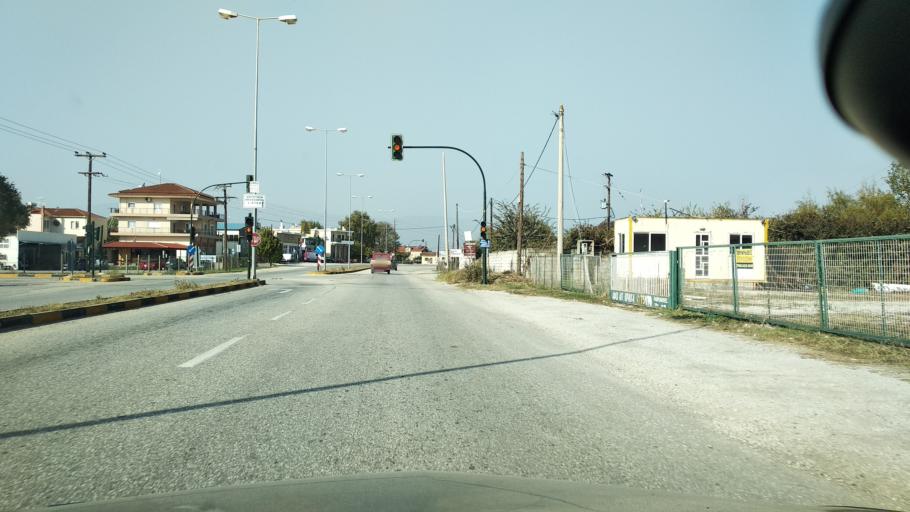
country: GR
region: Thessaly
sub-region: Trikala
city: Trikala
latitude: 39.5561
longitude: 21.7885
